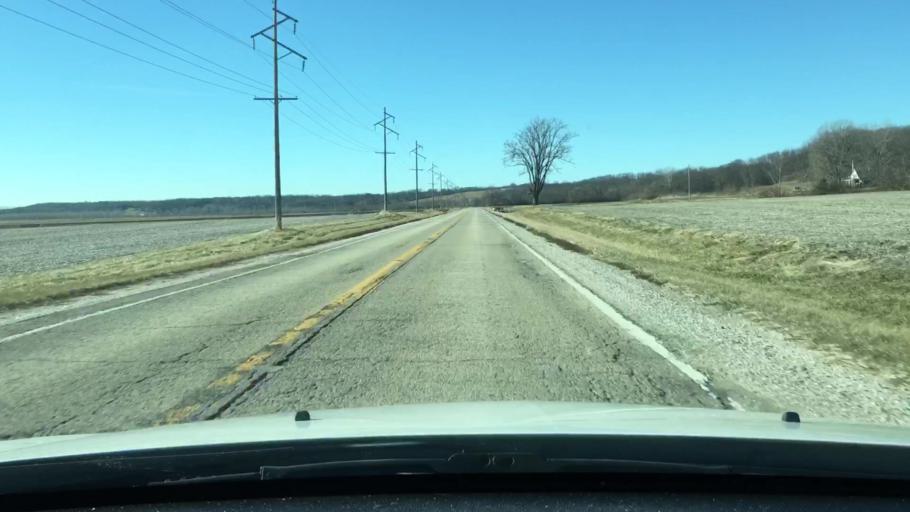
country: US
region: Illinois
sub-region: Fulton County
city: Astoria
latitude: 40.1752
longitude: -90.2608
